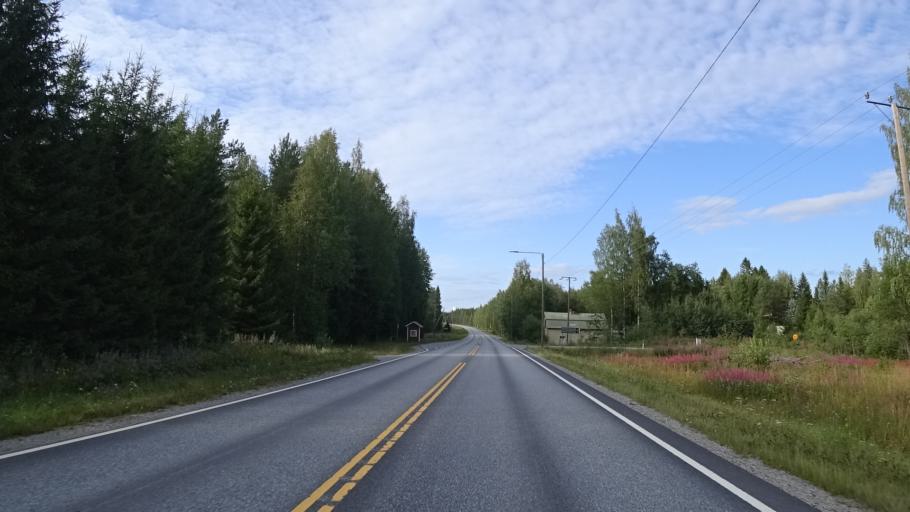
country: FI
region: North Karelia
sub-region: Joensuu
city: Eno
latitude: 62.8645
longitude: 30.1997
